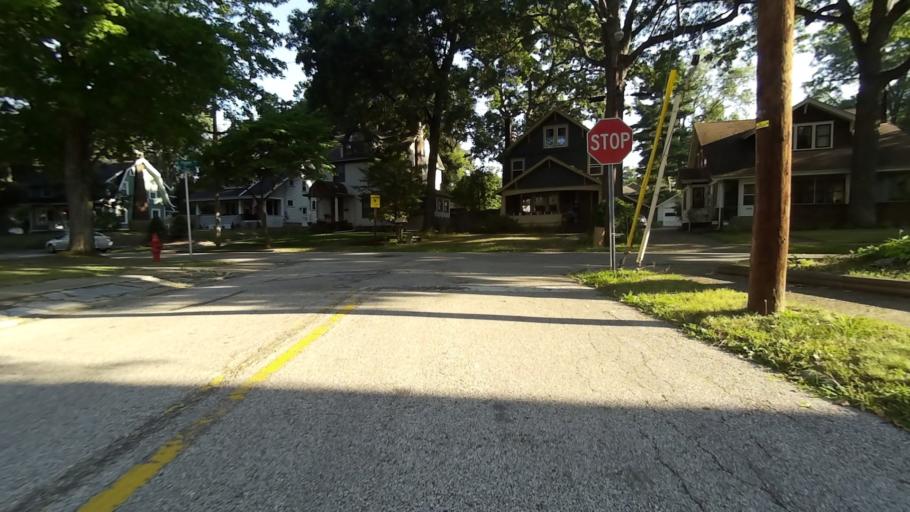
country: US
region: Ohio
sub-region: Portage County
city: Kent
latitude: 41.1552
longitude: -81.3657
